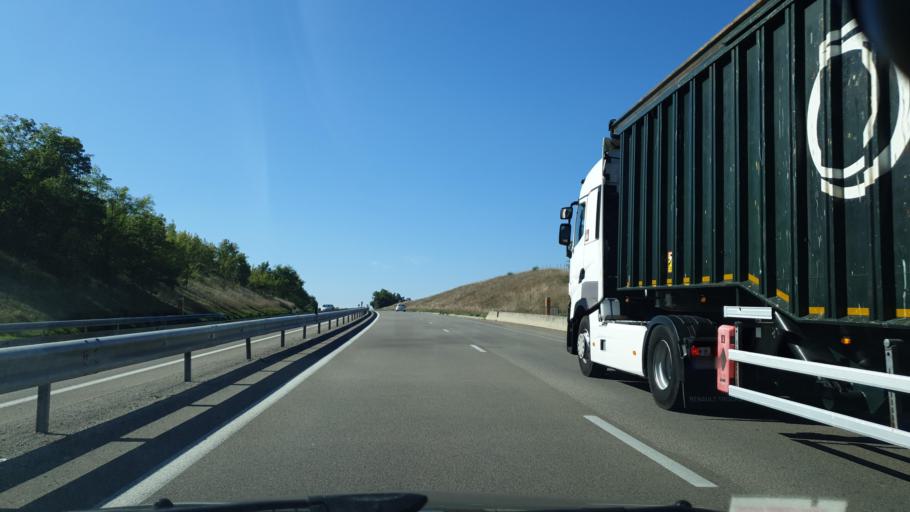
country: FR
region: Rhone-Alpes
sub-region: Departement de la Drome
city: Saint-Paul-les-Romans
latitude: 45.0415
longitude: 5.1474
